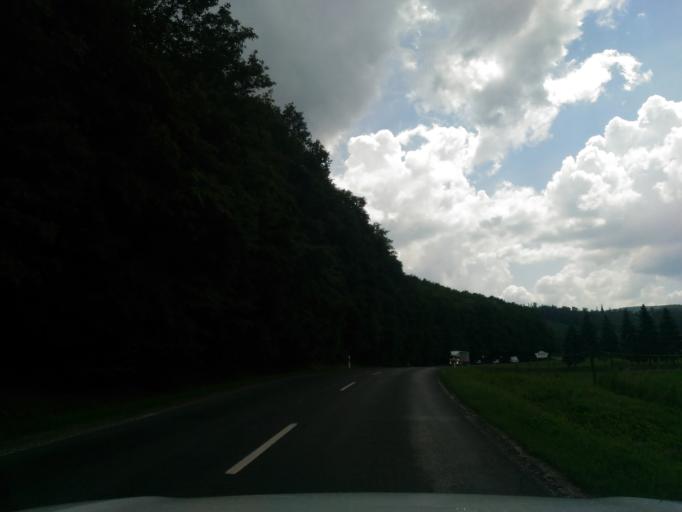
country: HU
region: Baranya
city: Komlo
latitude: 46.1672
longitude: 18.2152
